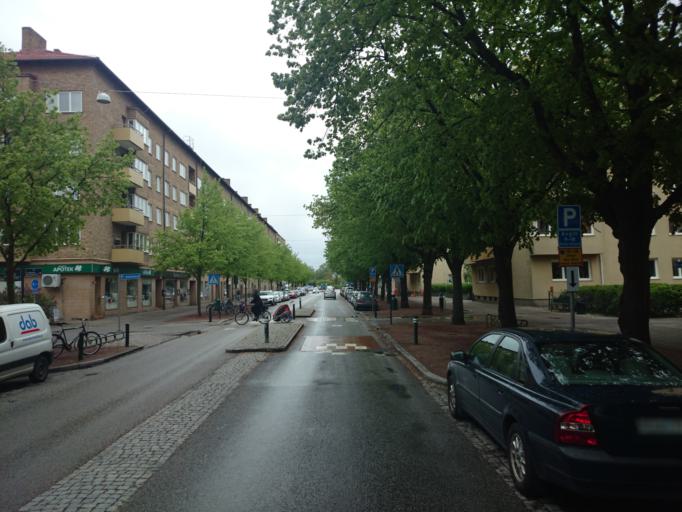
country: SE
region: Skane
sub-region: Malmo
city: Malmoe
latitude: 55.5981
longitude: 12.9749
